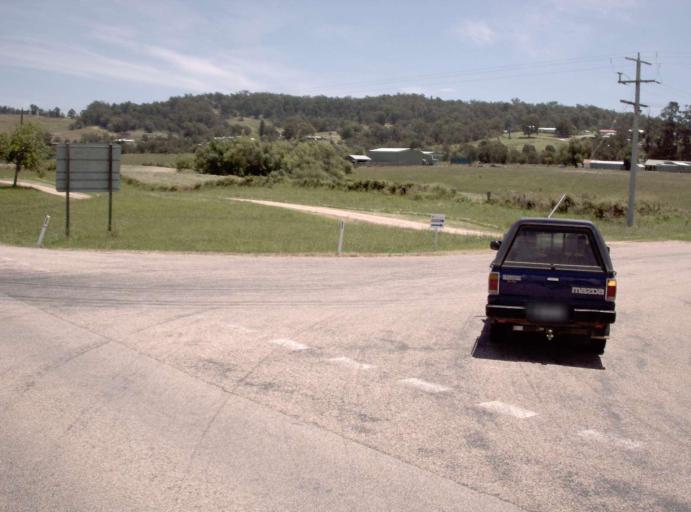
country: AU
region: Victoria
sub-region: East Gippsland
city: Lakes Entrance
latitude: -37.7088
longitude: 147.8259
